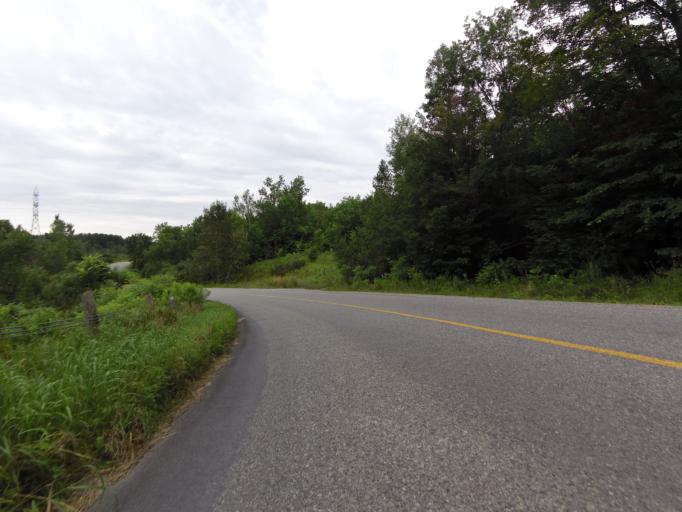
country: CA
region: Ontario
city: Kingston
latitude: 44.6063
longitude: -76.6428
